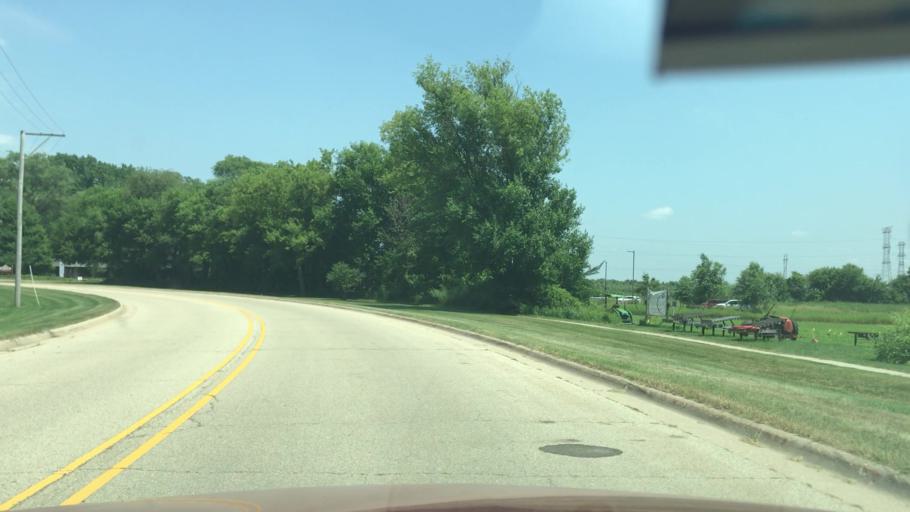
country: US
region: Illinois
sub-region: Winnebago County
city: Cherry Valley
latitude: 42.2348
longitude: -88.9466
